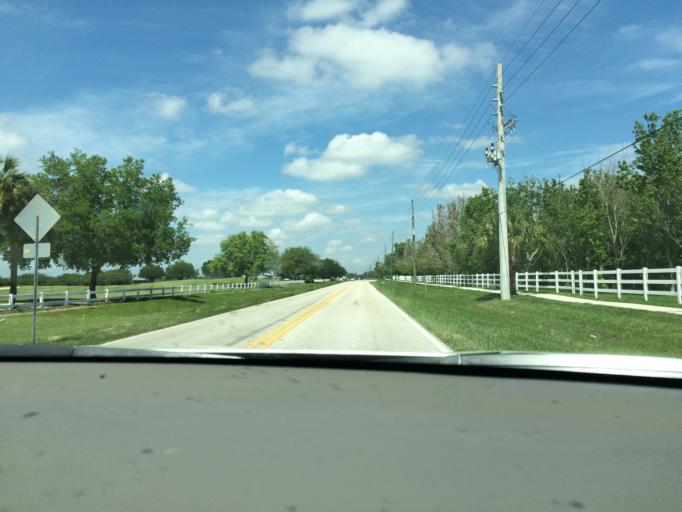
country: US
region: Florida
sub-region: Manatee County
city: Ellenton
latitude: 27.4961
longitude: -82.4337
